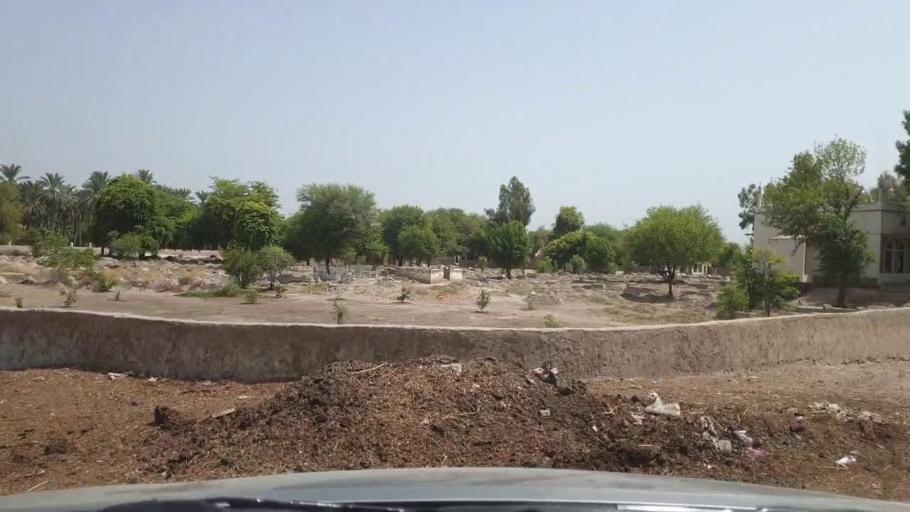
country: PK
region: Sindh
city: Pano Aqil
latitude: 27.9078
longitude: 69.1507
